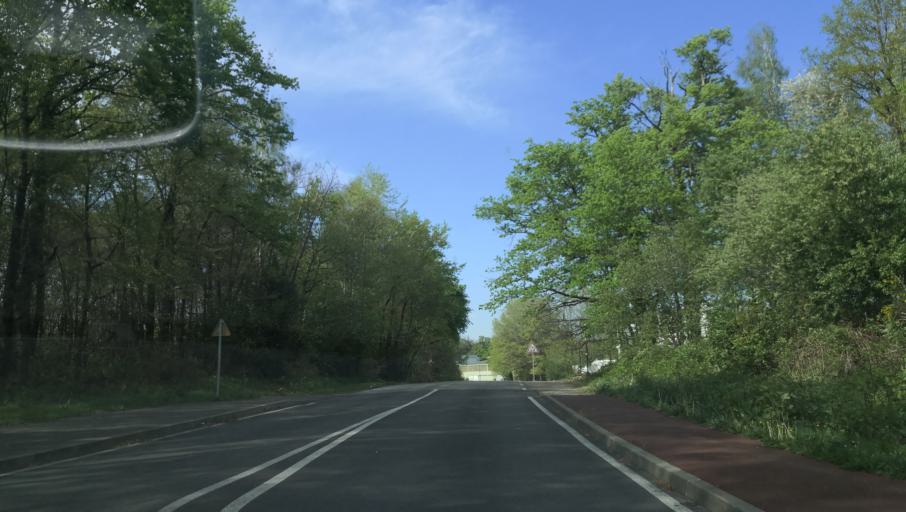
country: FR
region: Limousin
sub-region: Departement de la Haute-Vienne
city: Couzeix
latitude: 45.8670
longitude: 1.2591
